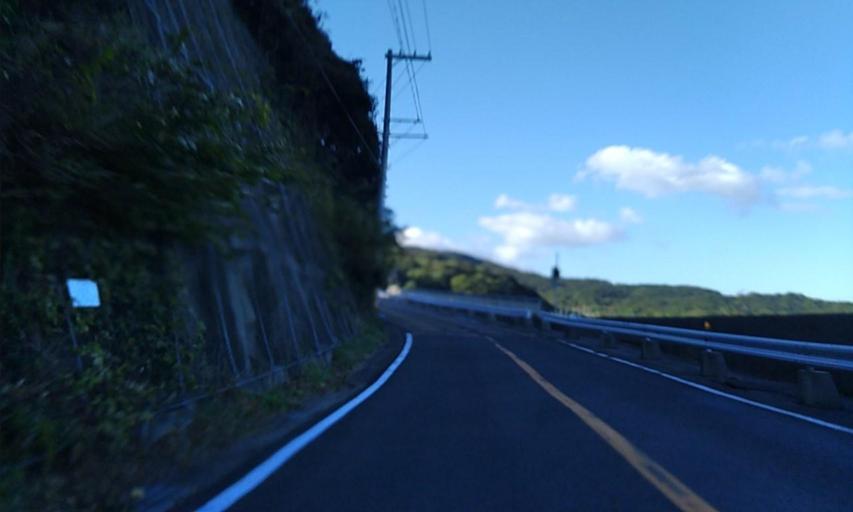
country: JP
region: Wakayama
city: Minato
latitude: 34.3094
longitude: 135.0895
